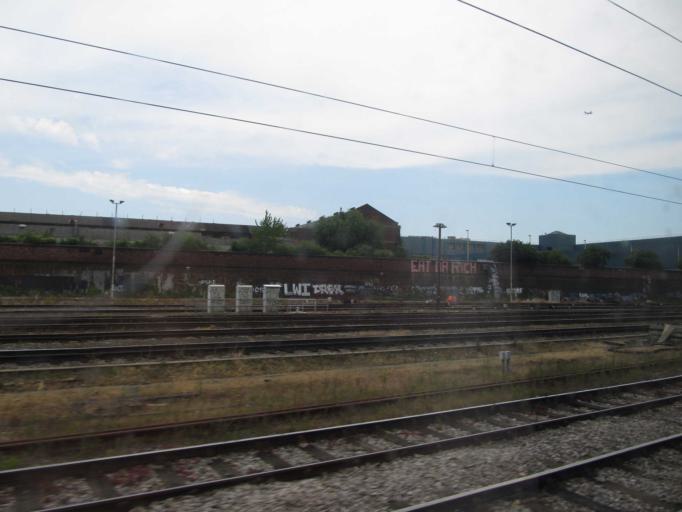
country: GB
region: England
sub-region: Greater London
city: Hammersmith
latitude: 51.5250
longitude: -0.2403
